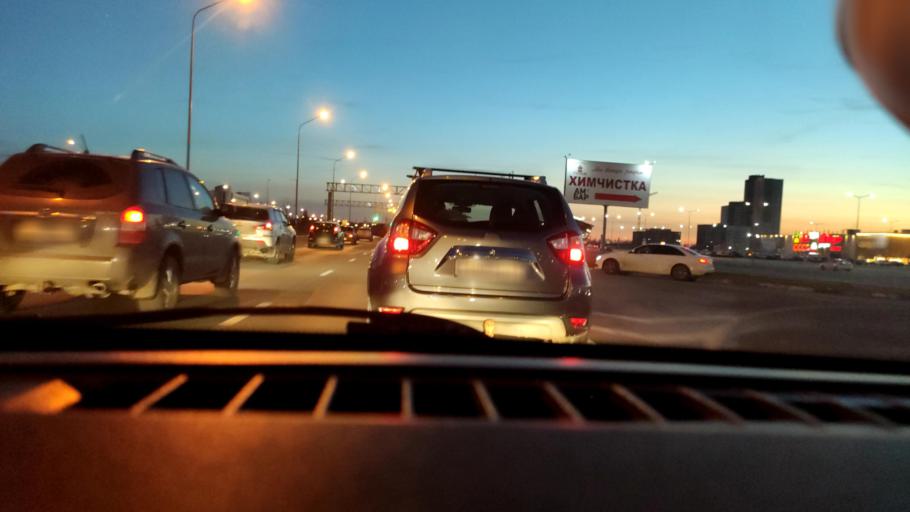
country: RU
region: Samara
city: Samara
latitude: 53.1396
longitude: 50.1773
